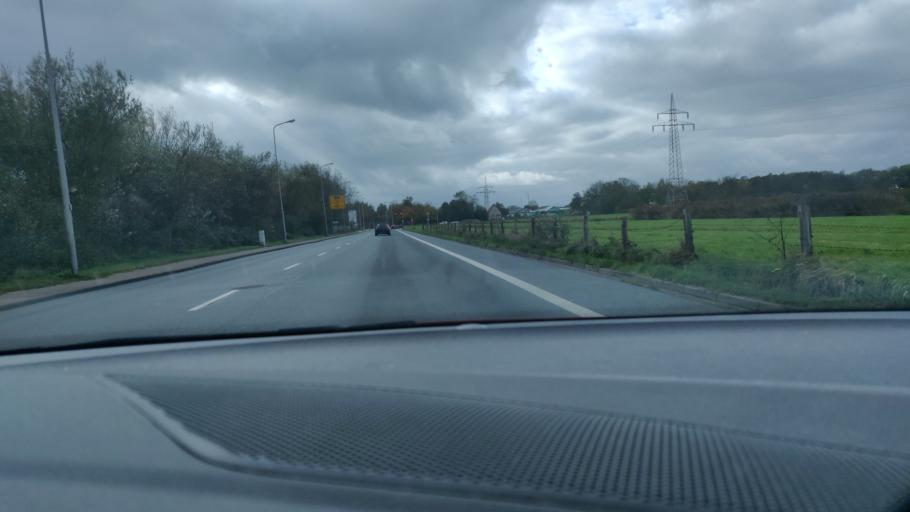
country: DE
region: Lower Saxony
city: Cuxhaven
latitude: 53.8628
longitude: 8.6741
